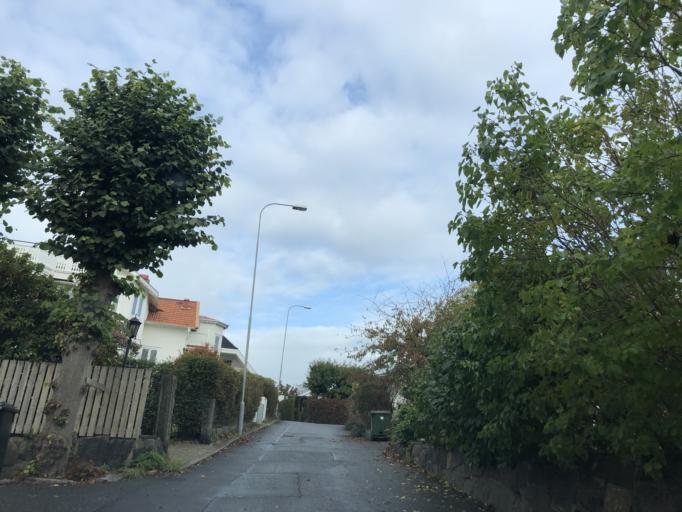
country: SE
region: Vaestra Goetaland
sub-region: Goteborg
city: Majorna
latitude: 57.6693
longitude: 11.8648
